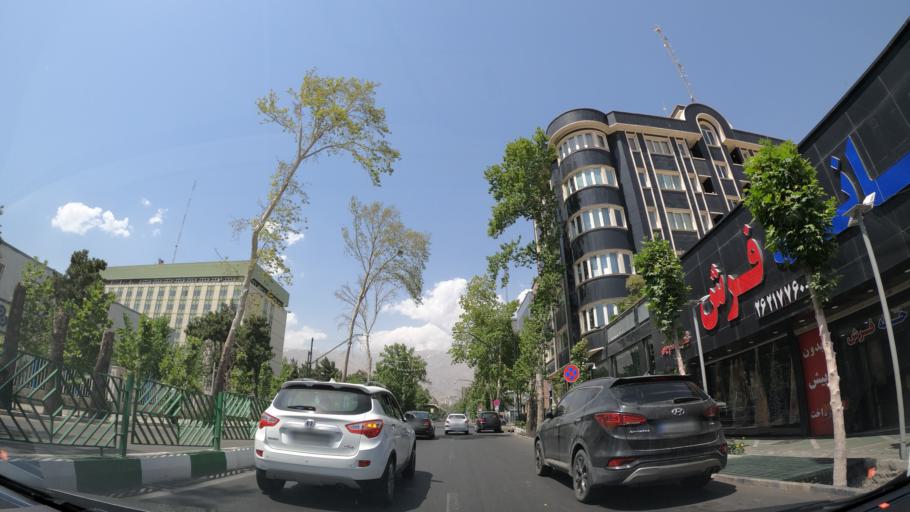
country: IR
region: Tehran
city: Tajrish
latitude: 35.7812
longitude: 51.4142
